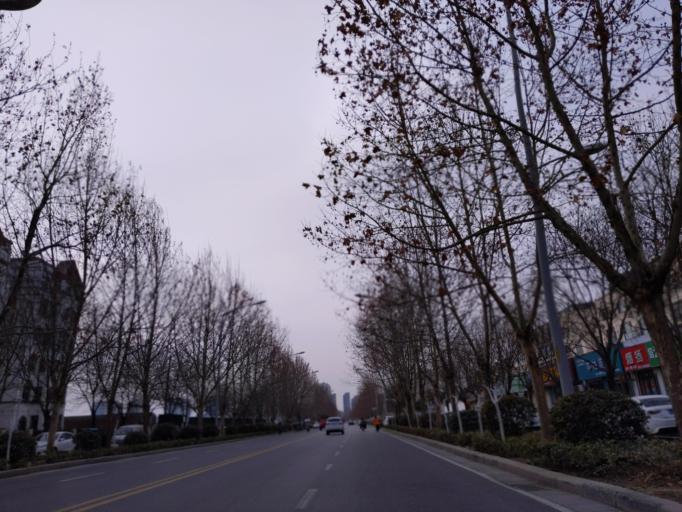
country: CN
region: Henan Sheng
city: Zhongyuanlu
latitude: 35.7577
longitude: 115.0513
